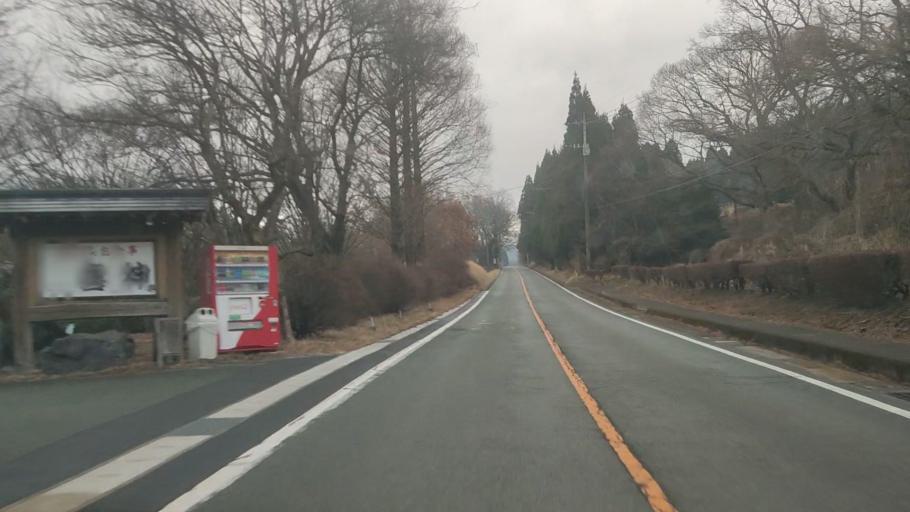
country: JP
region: Kumamoto
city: Aso
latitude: 32.8495
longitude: 131.1498
